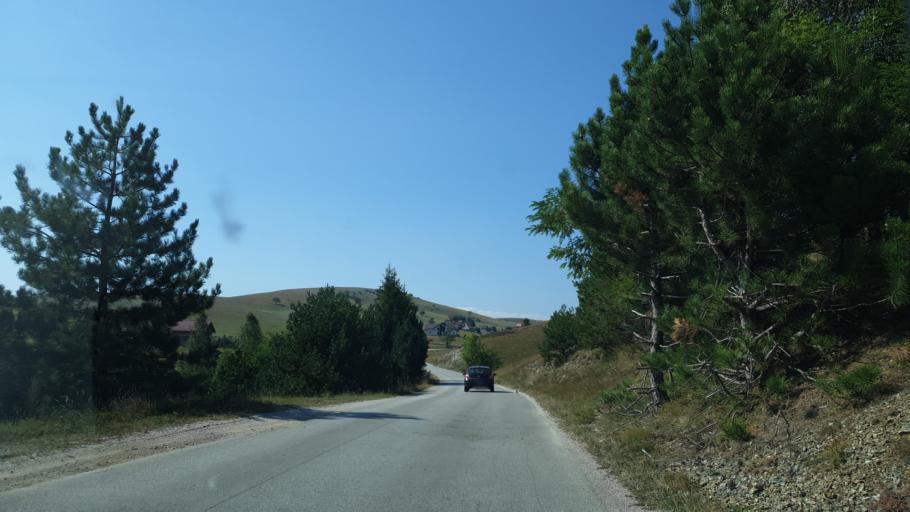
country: RS
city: Zlatibor
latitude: 43.7157
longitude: 19.7390
